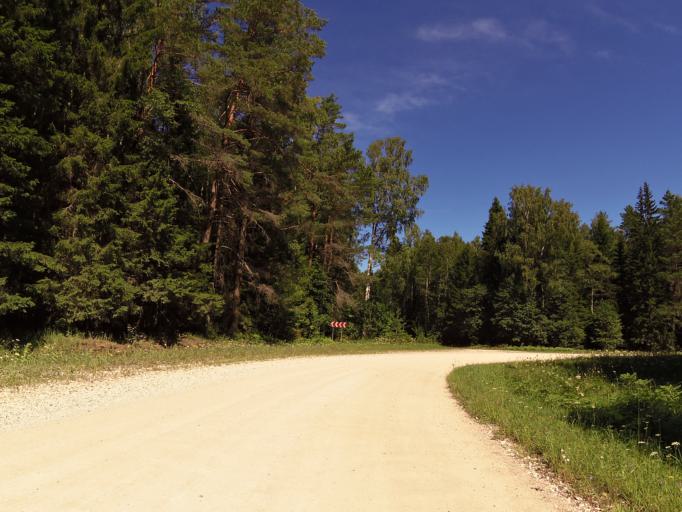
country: EE
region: Hiiumaa
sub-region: Kaerdla linn
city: Kardla
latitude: 58.9199
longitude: 22.3505
